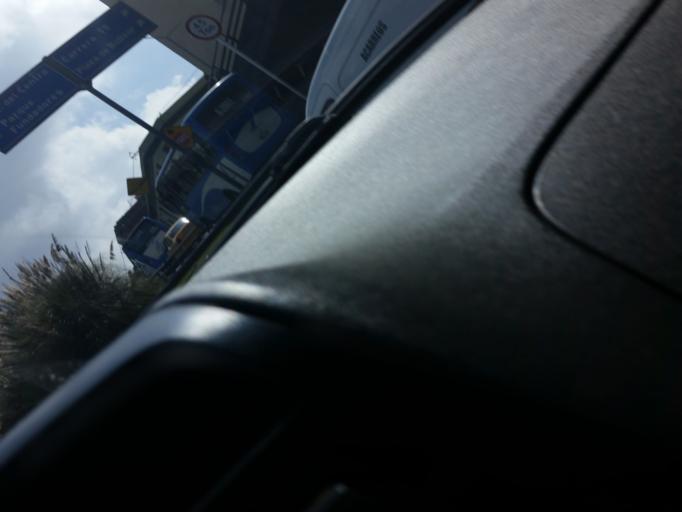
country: CO
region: Caldas
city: Manizales
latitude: 5.0698
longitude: -75.5181
